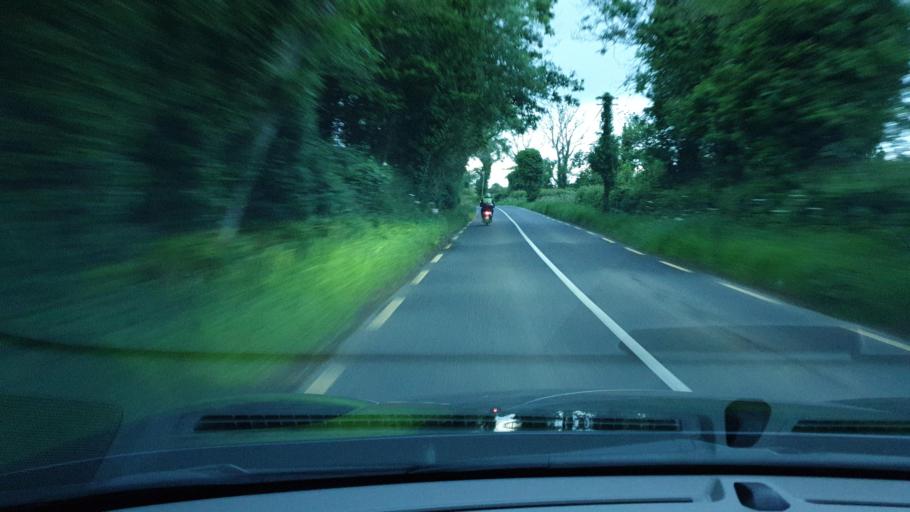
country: IE
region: Leinster
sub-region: An Mhi
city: Ashbourne
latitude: 53.5074
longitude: -6.3189
